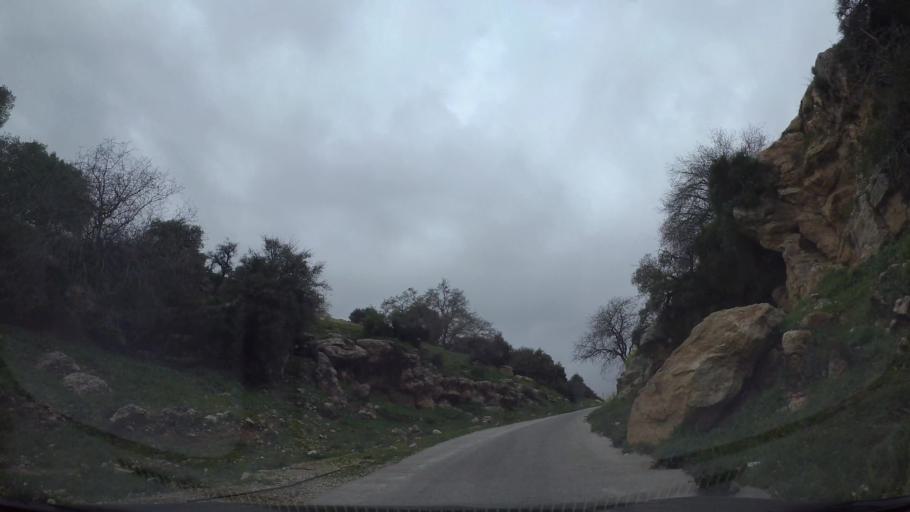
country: JO
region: Amman
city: Wadi as Sir
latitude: 31.9530
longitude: 35.8139
